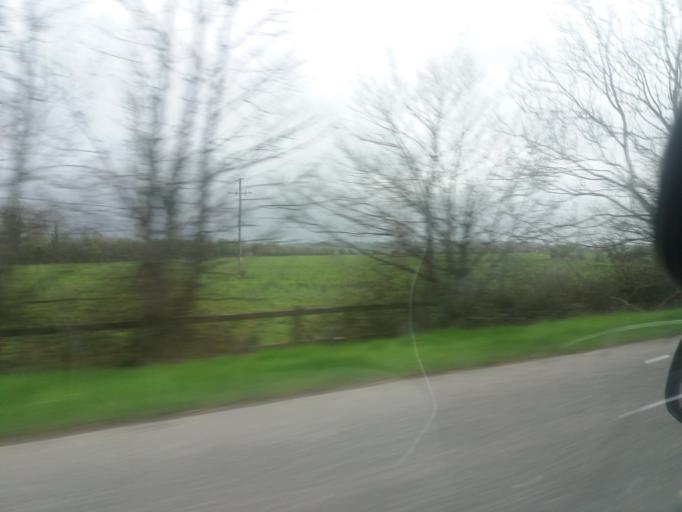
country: IE
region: Munster
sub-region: County Limerick
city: Rathkeale
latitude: 52.4975
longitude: -8.9953
